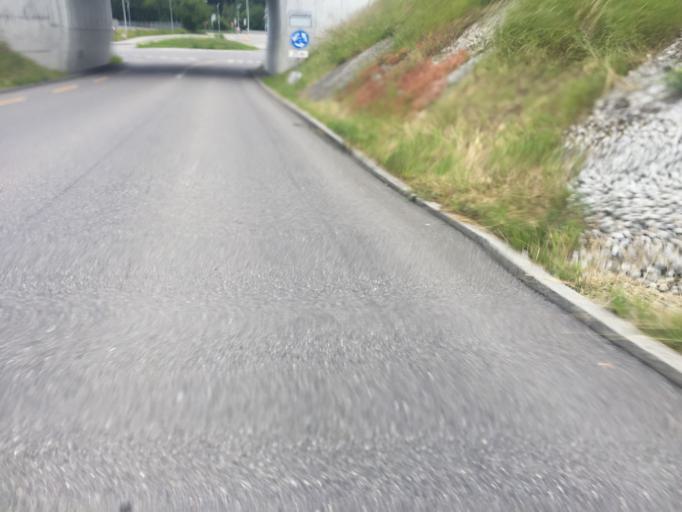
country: CH
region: Bern
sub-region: Bern-Mittelland District
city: Wohlen
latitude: 46.9424
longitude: 7.3700
